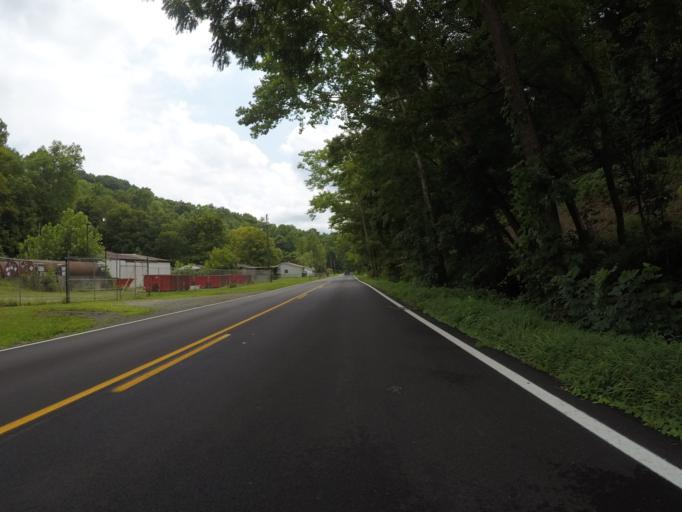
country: US
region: Kentucky
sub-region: Boyd County
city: Catlettsburg
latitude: 38.4214
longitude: -82.6246
